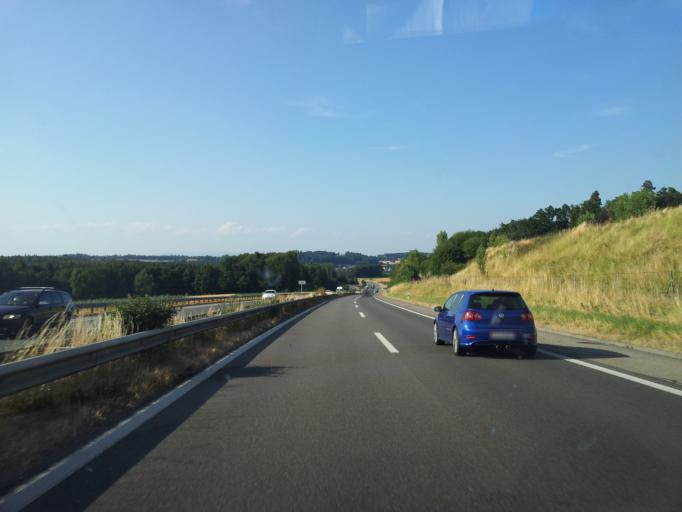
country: CH
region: Fribourg
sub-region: Sarine District
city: Matran
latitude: 46.7646
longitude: 7.0910
